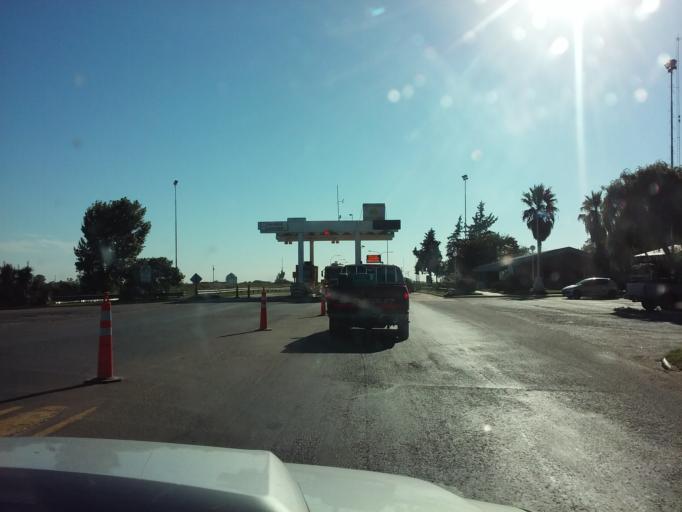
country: AR
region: Buenos Aires
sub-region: Partido de Trenque Lauquen
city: Trenque Lauquen
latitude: -35.9185
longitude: -62.5568
